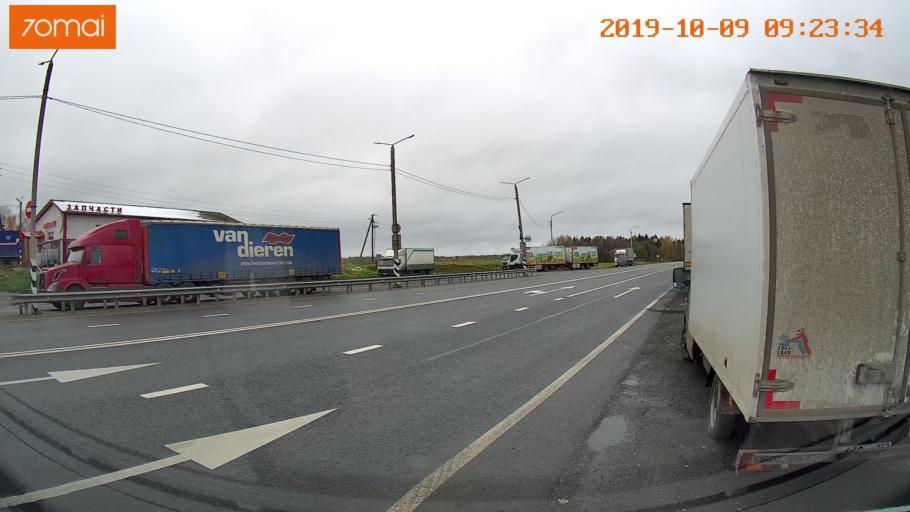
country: RU
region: Vologda
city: Vologda
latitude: 59.0726
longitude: 40.0273
